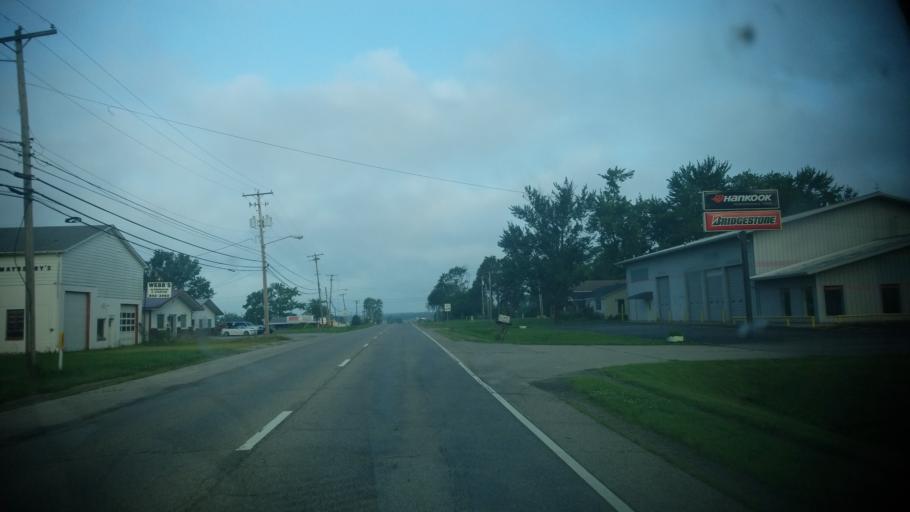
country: US
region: Illinois
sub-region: Wayne County
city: Fairfield
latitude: 38.3797
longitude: -88.3851
